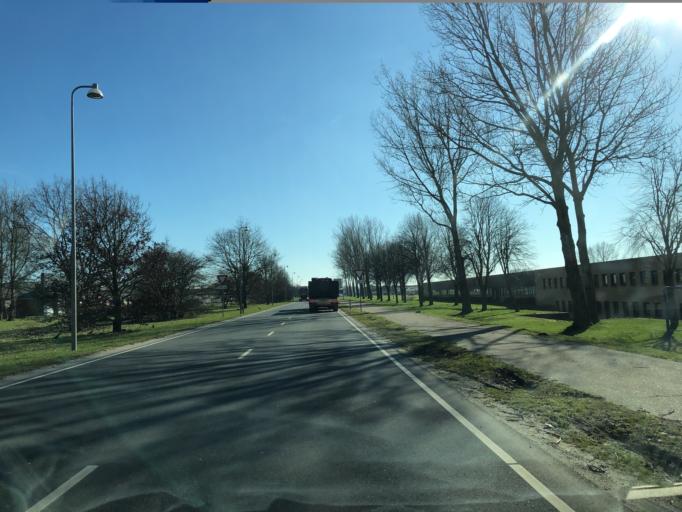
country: DK
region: Central Jutland
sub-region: Ikast-Brande Kommune
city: Ikast
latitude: 56.1303
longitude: 9.1675
